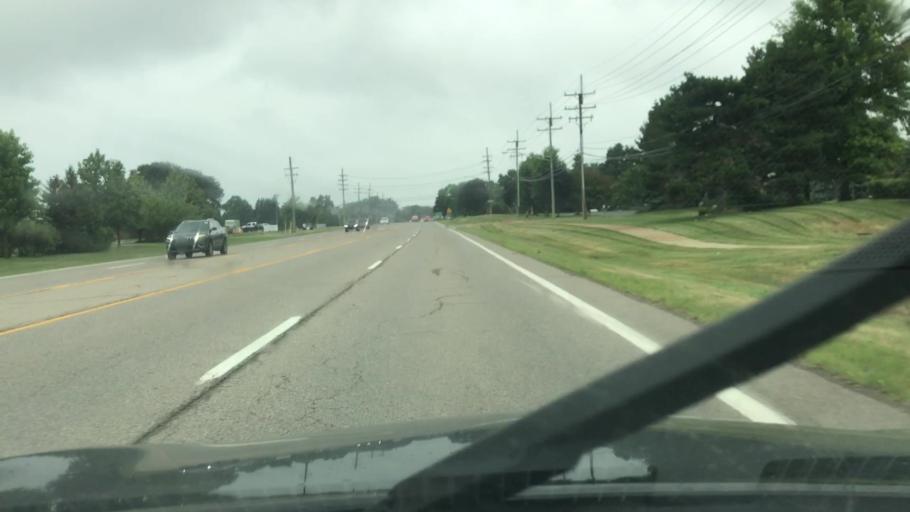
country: US
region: Michigan
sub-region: Oakland County
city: Wixom
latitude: 42.5172
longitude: -83.5372
